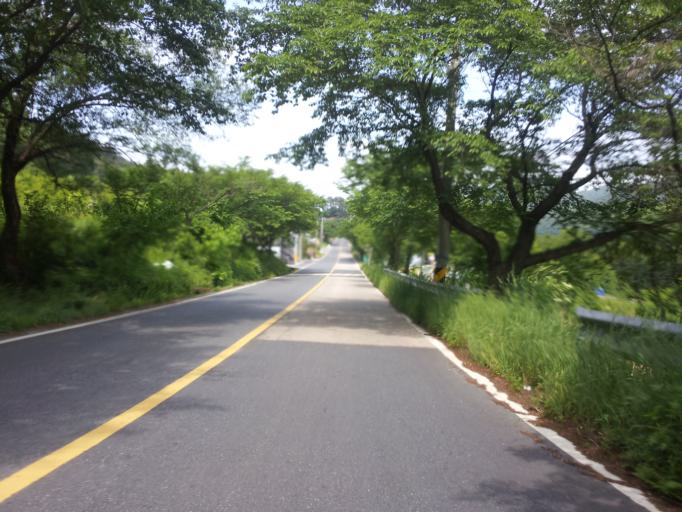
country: KR
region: Daejeon
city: Sintansin
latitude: 36.4253
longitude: 127.4634
